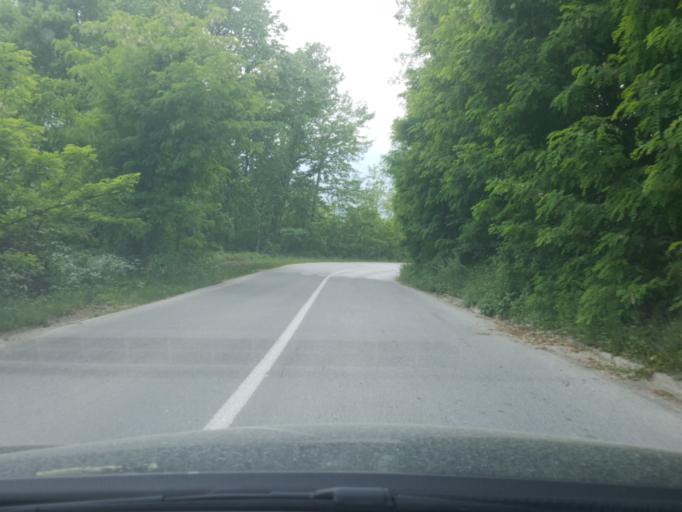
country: RS
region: Central Serbia
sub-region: Zlatiborski Okrug
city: Bajina Basta
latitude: 43.9433
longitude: 19.5621
